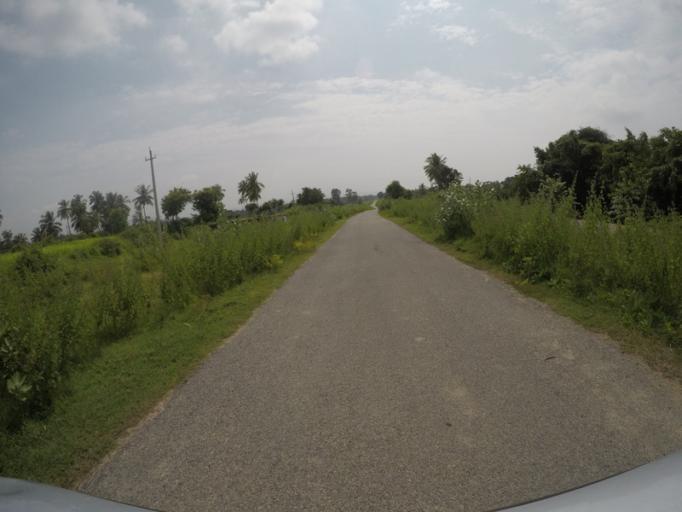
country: IN
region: Karnataka
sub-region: Ramanagara
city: Kanakapura
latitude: 12.4627
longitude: 77.3323
